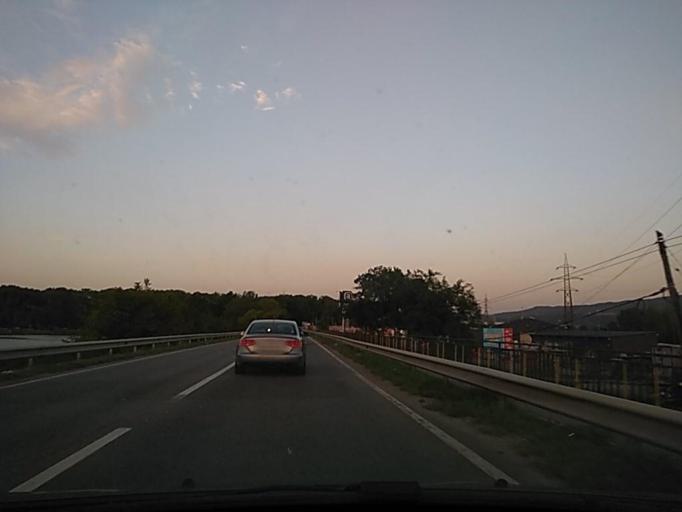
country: RO
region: Valcea
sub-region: Municipiul Ramnicu Valcea
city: Ramnicu Valcea
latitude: 45.0731
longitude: 24.3533
